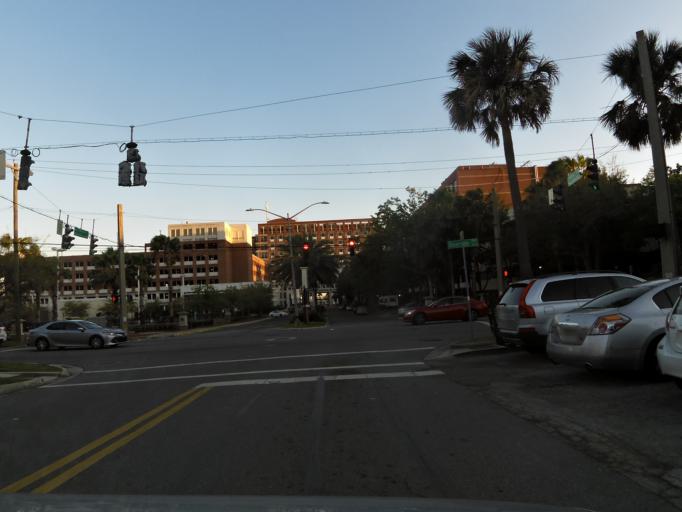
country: US
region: Florida
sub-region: Duval County
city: Jacksonville
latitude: 30.3095
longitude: -81.6896
